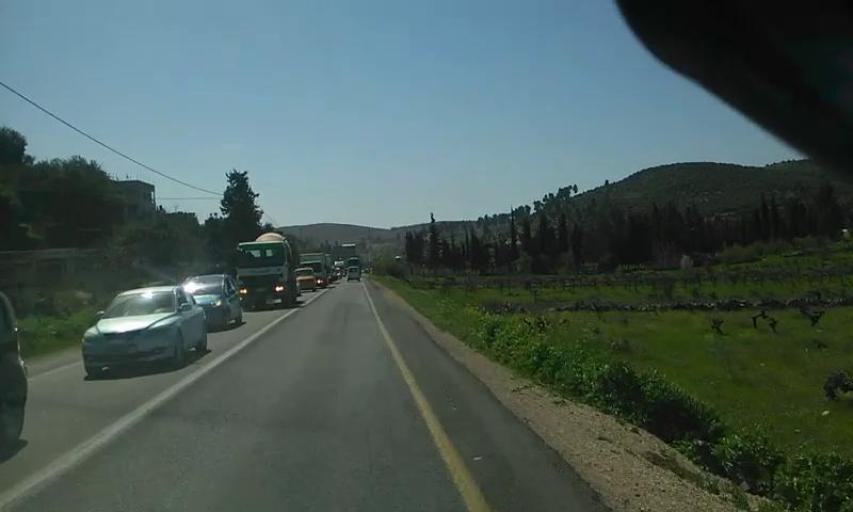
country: PS
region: West Bank
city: Shuyukh al `Arrub
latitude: 31.6289
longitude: 35.1324
